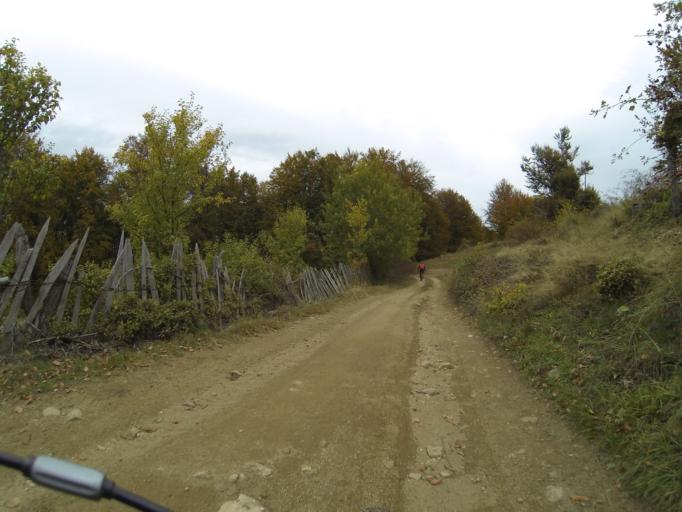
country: RO
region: Gorj
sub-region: Comuna Pades
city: Closani
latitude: 45.0960
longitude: 22.8388
